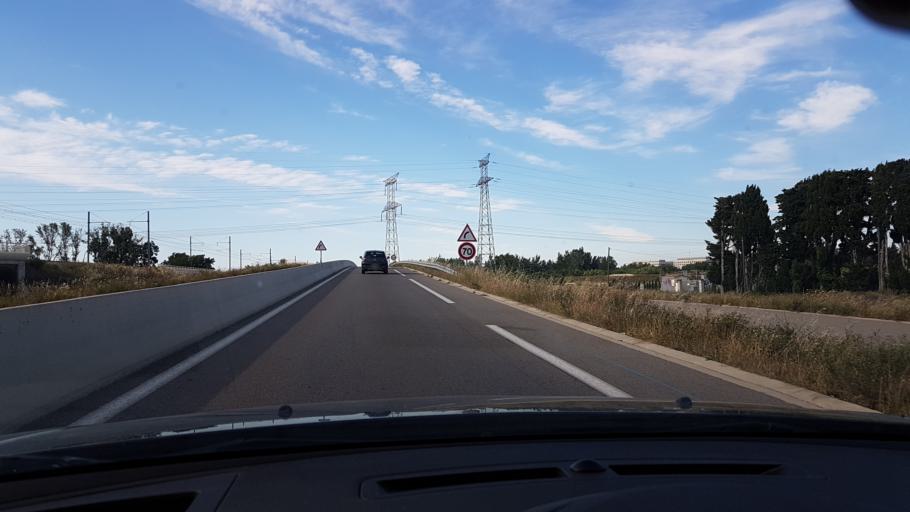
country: FR
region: Provence-Alpes-Cote d'Azur
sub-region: Departement des Bouches-du-Rhone
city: Rognonas
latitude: 43.9119
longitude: 4.7923
